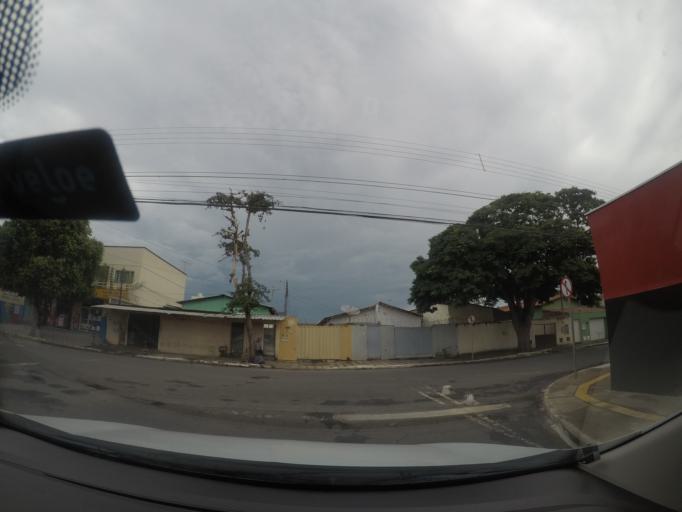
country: BR
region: Goias
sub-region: Goiania
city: Goiania
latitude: -16.6700
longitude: -49.2831
